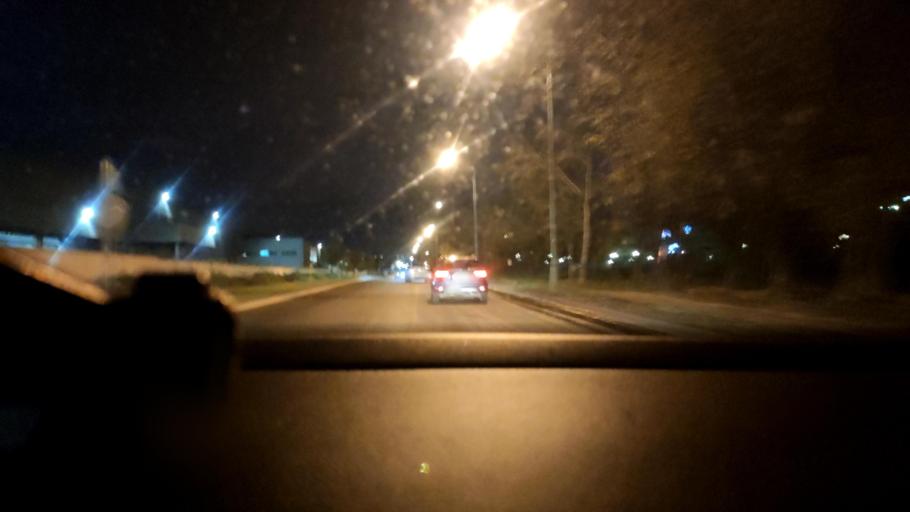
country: RU
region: Moskovskaya
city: Kur'yanovo
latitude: 55.6480
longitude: 37.6907
